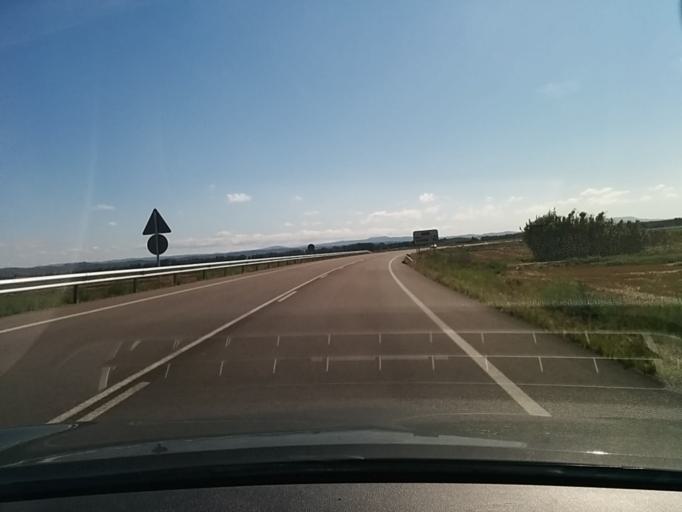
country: ES
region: Aragon
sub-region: Provincia de Zaragoza
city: Ejea de los Caballeros
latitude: 42.1393
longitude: -1.1355
